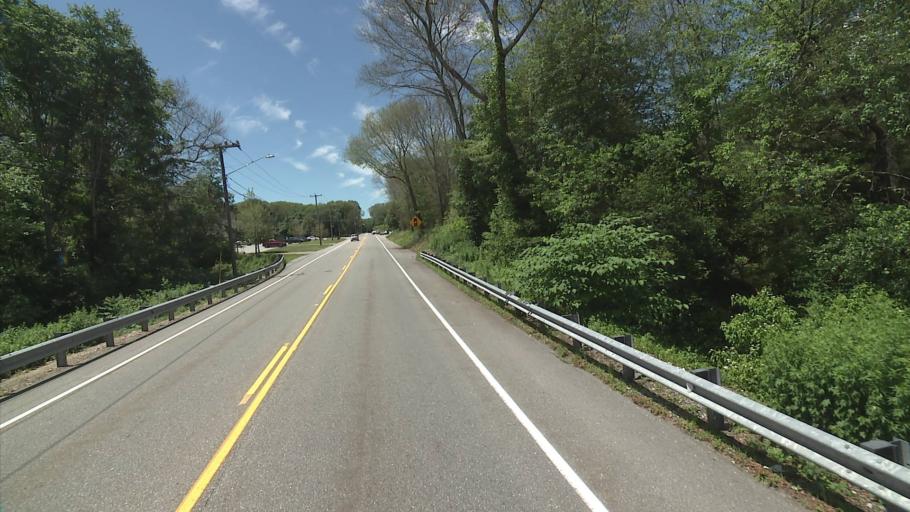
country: US
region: Connecticut
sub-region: New London County
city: Old Mystic
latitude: 41.3945
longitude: -71.9611
